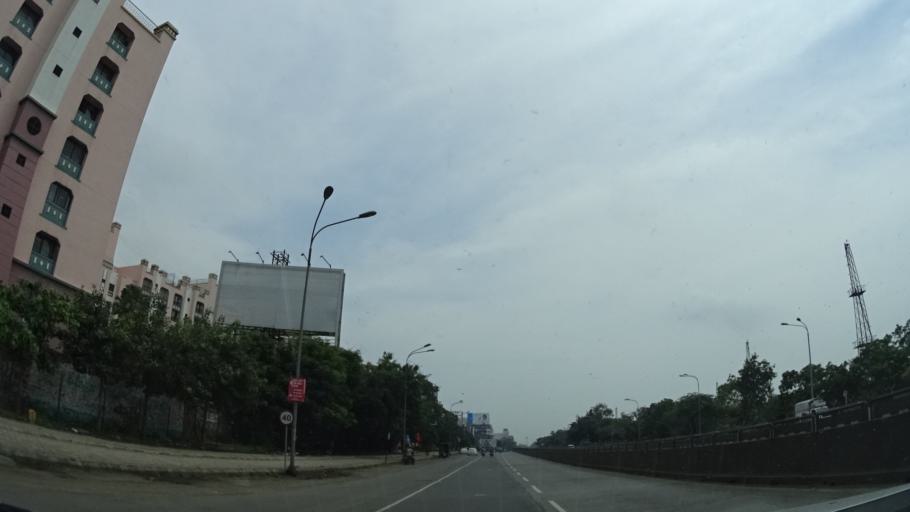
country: IN
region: Maharashtra
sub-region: Pune Division
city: Lohogaon
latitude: 18.5595
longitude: 73.9139
